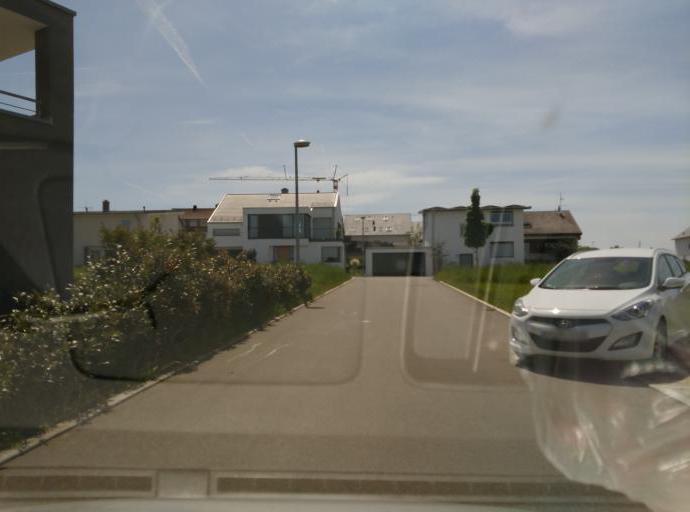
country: DE
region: Baden-Wuerttemberg
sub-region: Regierungsbezirk Stuttgart
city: Altdorf
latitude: 48.5974
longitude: 9.2722
